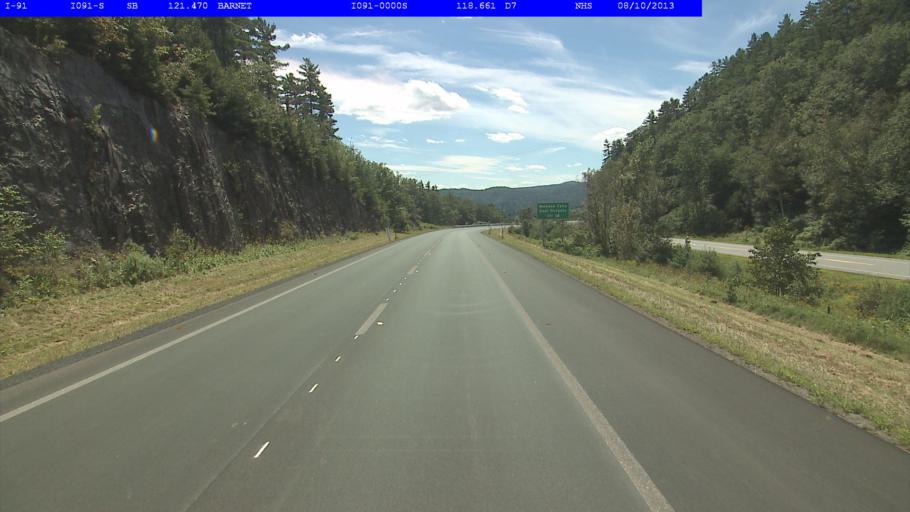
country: US
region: Vermont
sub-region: Caledonia County
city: Saint Johnsbury
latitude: 44.3042
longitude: -72.0391
